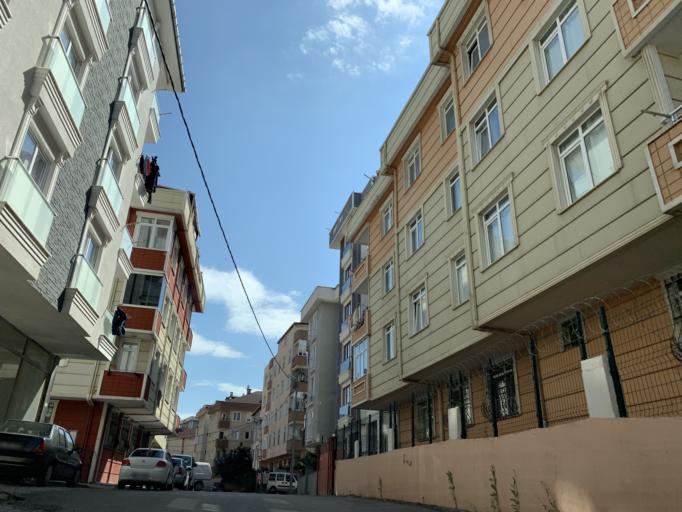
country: TR
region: Istanbul
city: Pendik
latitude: 40.8921
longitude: 29.2723
